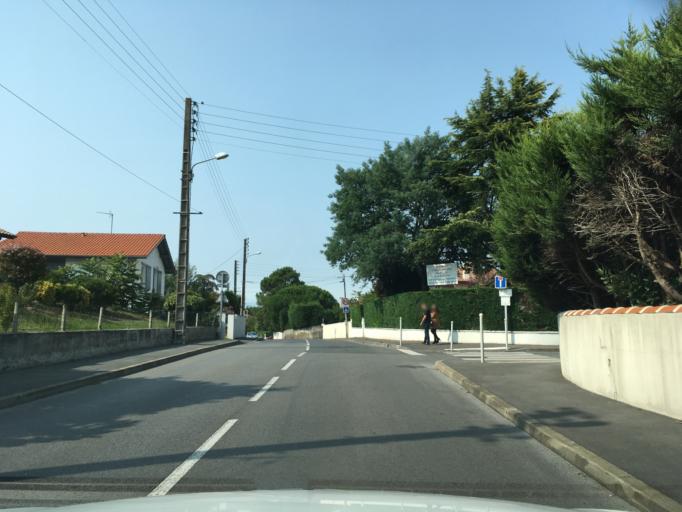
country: FR
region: Aquitaine
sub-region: Departement des Pyrenees-Atlantiques
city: Bayonne
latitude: 43.5093
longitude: -1.5027
